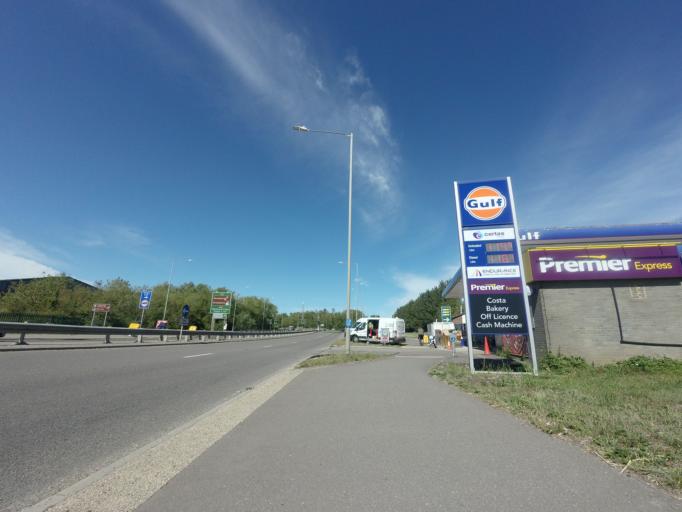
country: GB
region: England
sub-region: Kent
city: Sandwich
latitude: 51.3106
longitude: 1.3497
